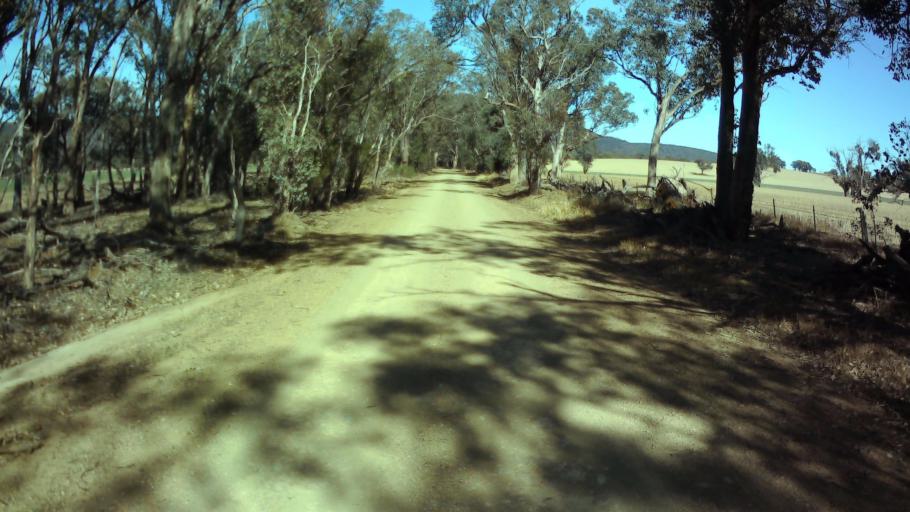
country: AU
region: New South Wales
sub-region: Weddin
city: Grenfell
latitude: -33.9016
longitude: 148.0309
